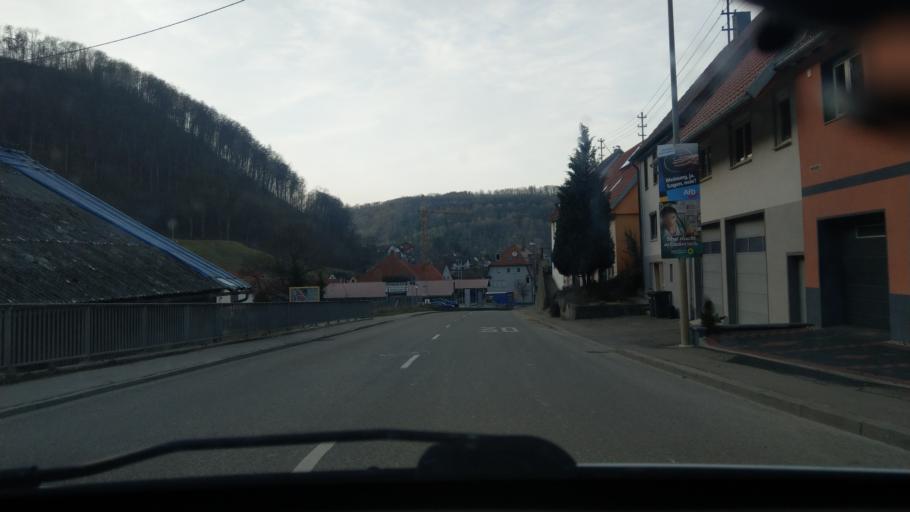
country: DE
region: Baden-Wuerttemberg
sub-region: Regierungsbezirk Stuttgart
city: Bohmenkirch
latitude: 48.7040
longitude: 9.8890
